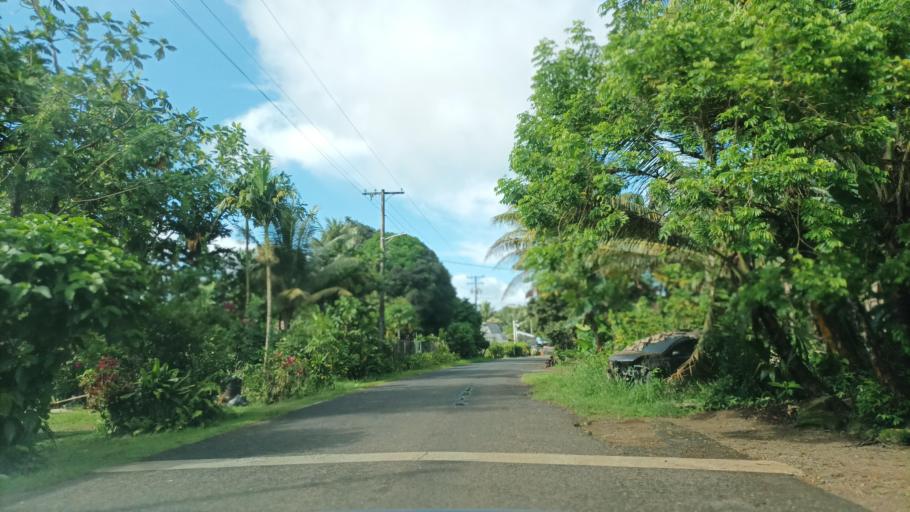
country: FM
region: Pohnpei
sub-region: Kolonia Municipality
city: Kolonia Town
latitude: 6.9649
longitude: 158.2044
